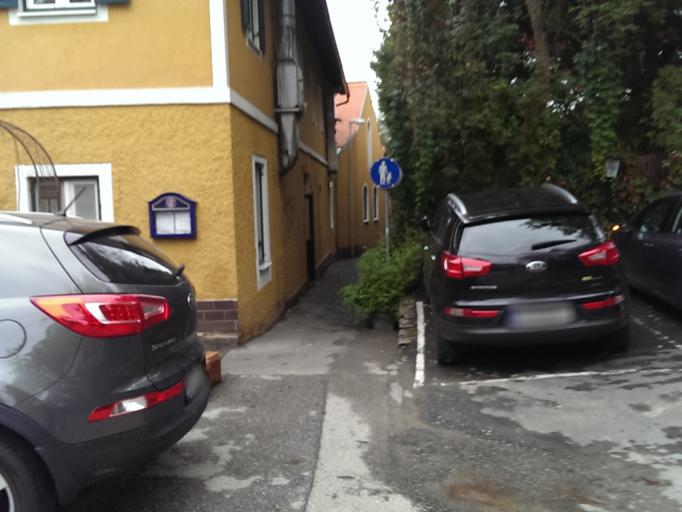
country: AT
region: Styria
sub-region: Graz Stadt
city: Graz
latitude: 47.0563
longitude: 15.4751
